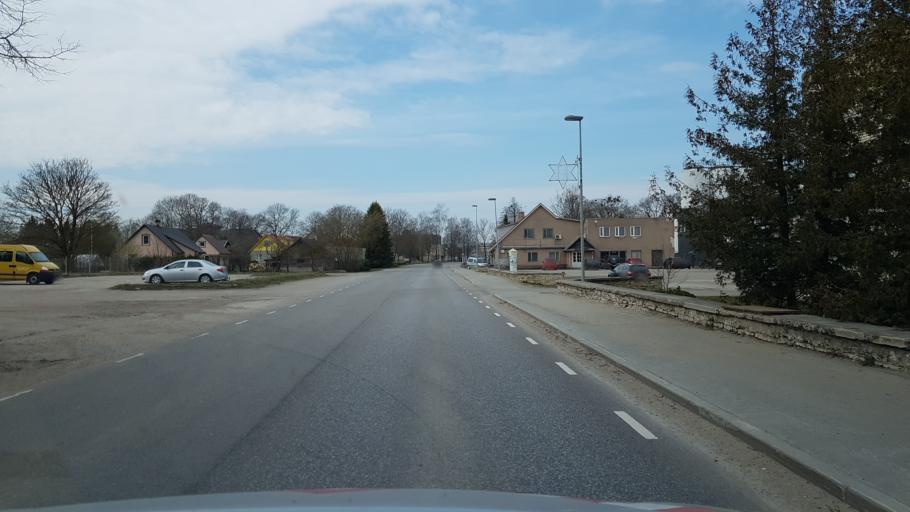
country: EE
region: Laeaene-Virumaa
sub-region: Haljala vald
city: Haljala
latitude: 59.4286
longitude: 26.2683
